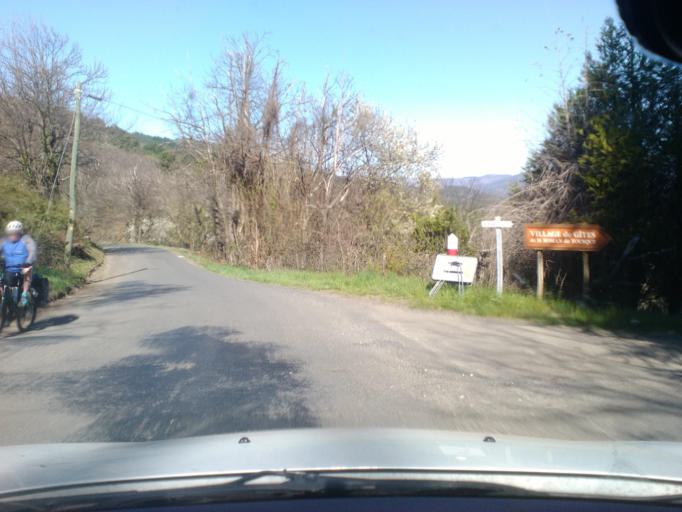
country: FR
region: Languedoc-Roussillon
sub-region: Departement du Gard
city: Saint-Jean-du-Gard
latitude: 44.1505
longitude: 3.7693
